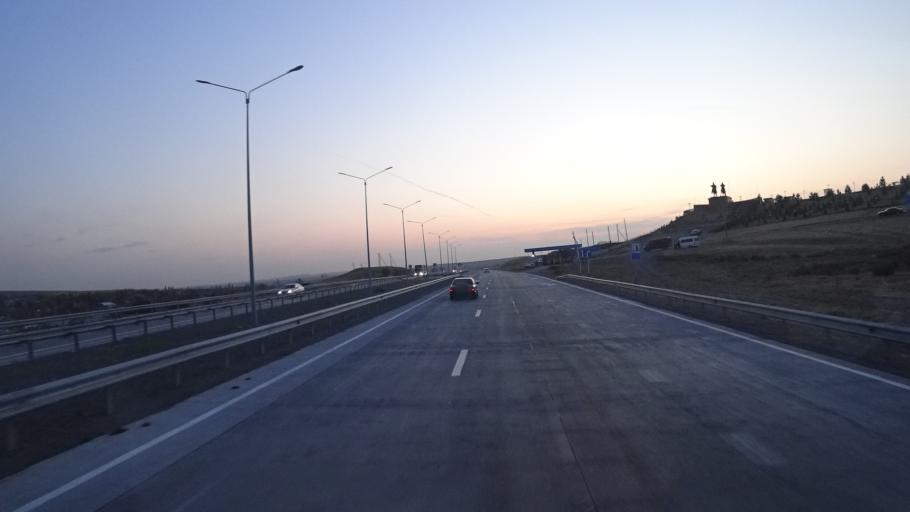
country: KZ
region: Ongtustik Qazaqstan
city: Qazyqurt
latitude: 41.8753
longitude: 69.4295
